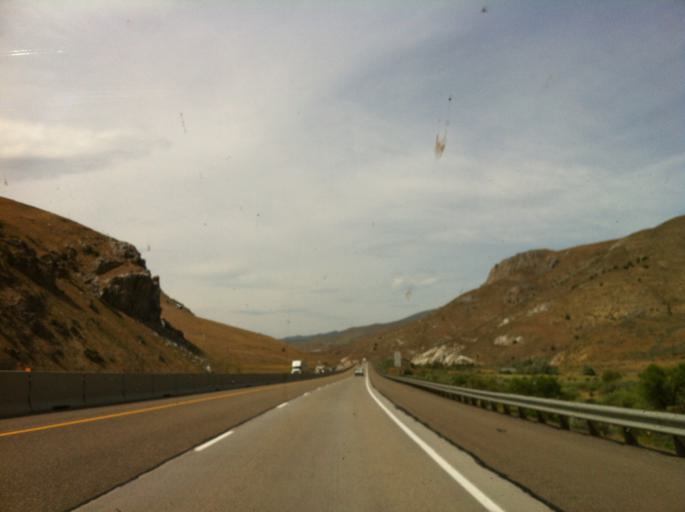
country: US
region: Idaho
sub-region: Washington County
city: Weiser
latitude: 44.3684
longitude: -117.2956
